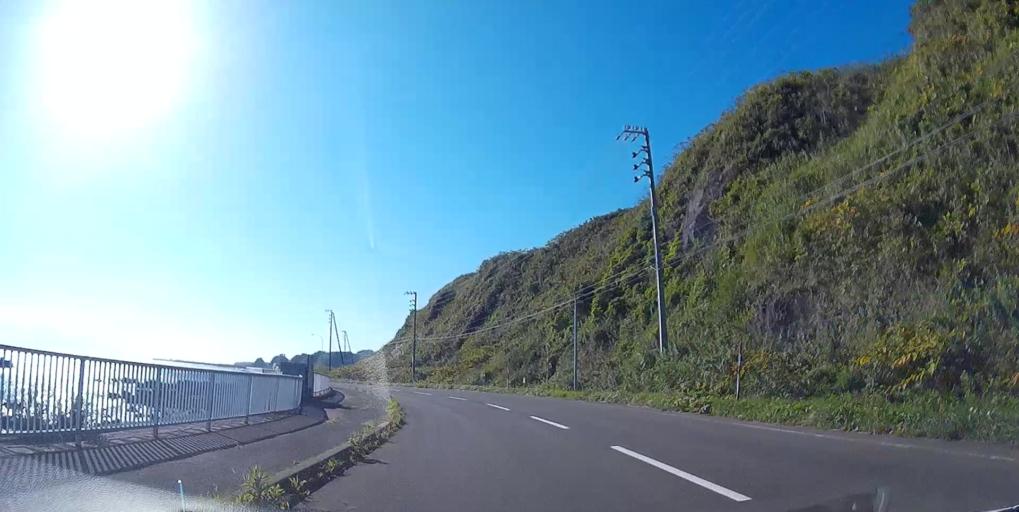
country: JP
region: Hokkaido
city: Kamiiso
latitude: 42.2172
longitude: 139.8524
